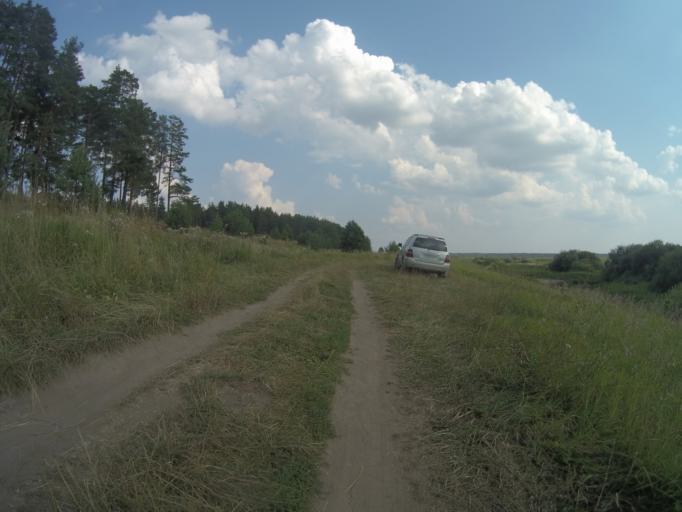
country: RU
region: Vladimir
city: Orgtrud
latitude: 56.3201
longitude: 40.6811
